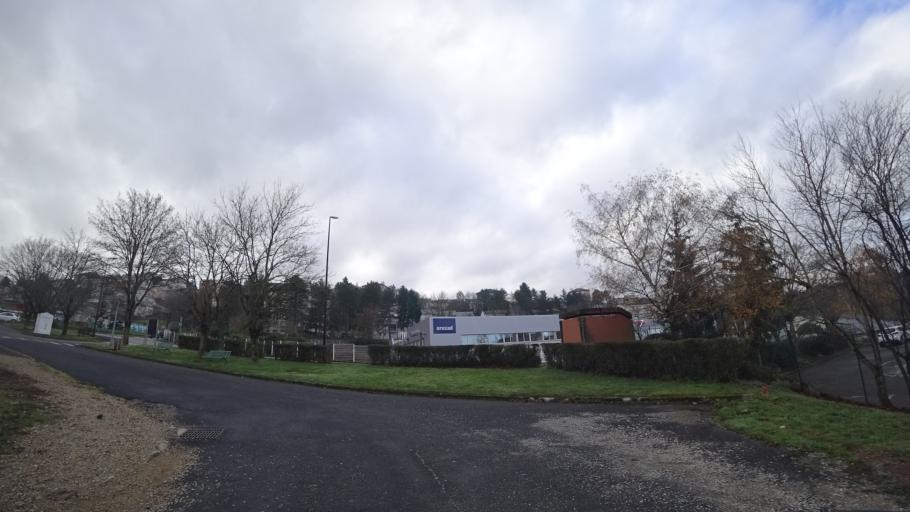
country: FR
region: Midi-Pyrenees
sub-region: Departement de l'Aveyron
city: Rodez
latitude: 44.3606
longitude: 2.5716
